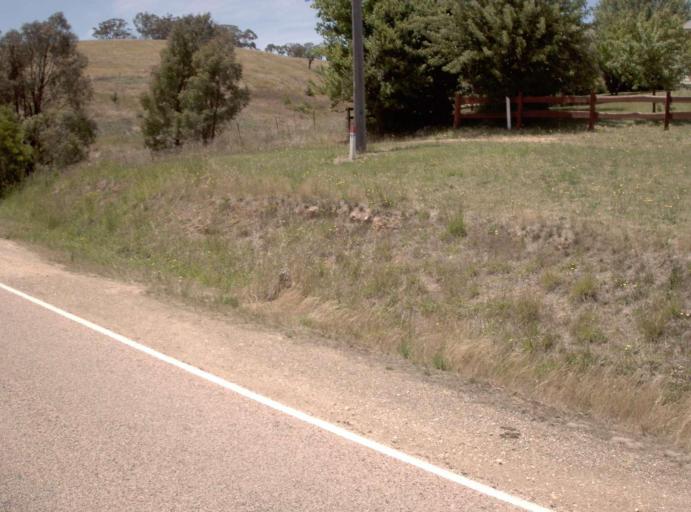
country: AU
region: Victoria
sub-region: Alpine
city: Mount Beauty
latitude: -37.1028
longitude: 147.5861
